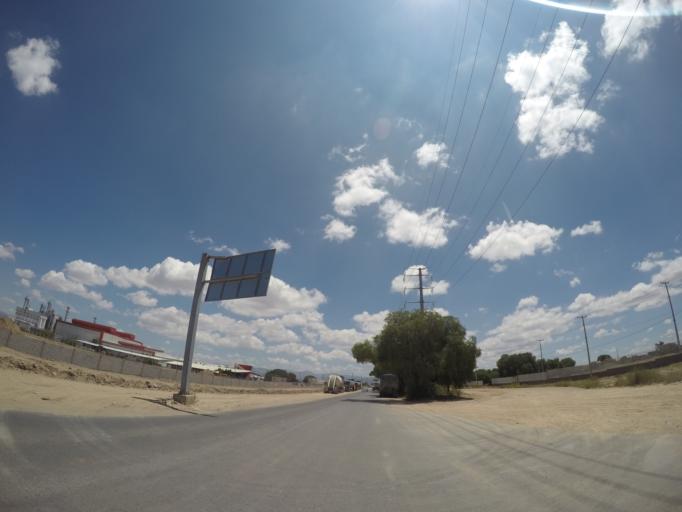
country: MX
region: San Luis Potosi
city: La Pila
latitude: 22.0432
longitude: -100.8991
